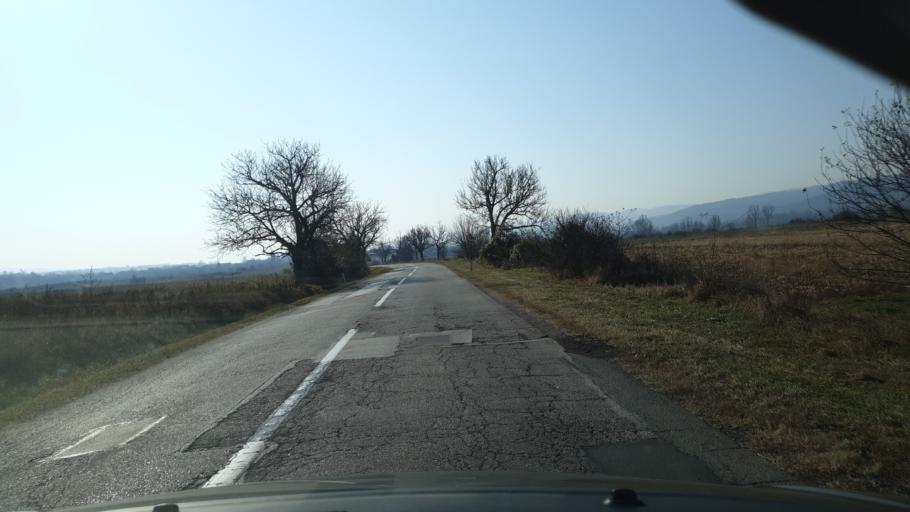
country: RS
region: Central Serbia
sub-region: Zajecarski Okrug
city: Knjazevac
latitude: 43.6967
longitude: 22.2975
